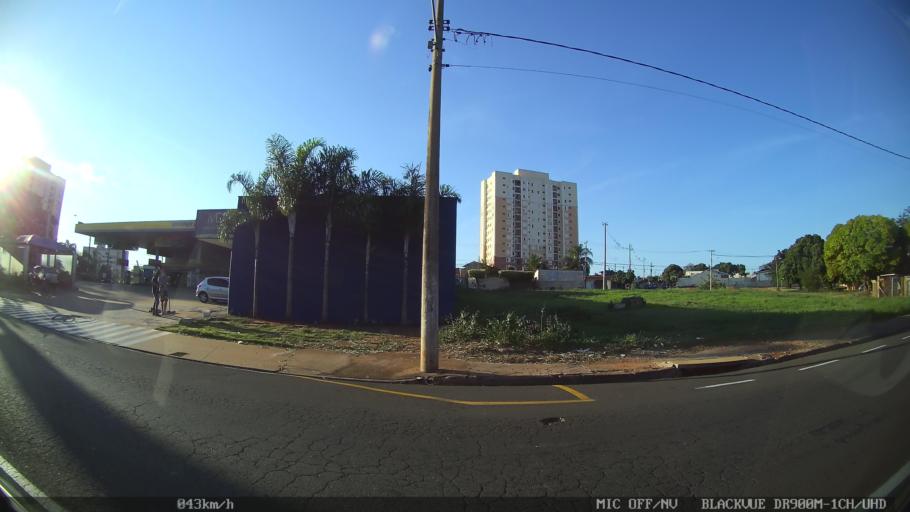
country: BR
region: Sao Paulo
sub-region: Sao Jose Do Rio Preto
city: Sao Jose do Rio Preto
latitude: -20.7868
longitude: -49.3677
